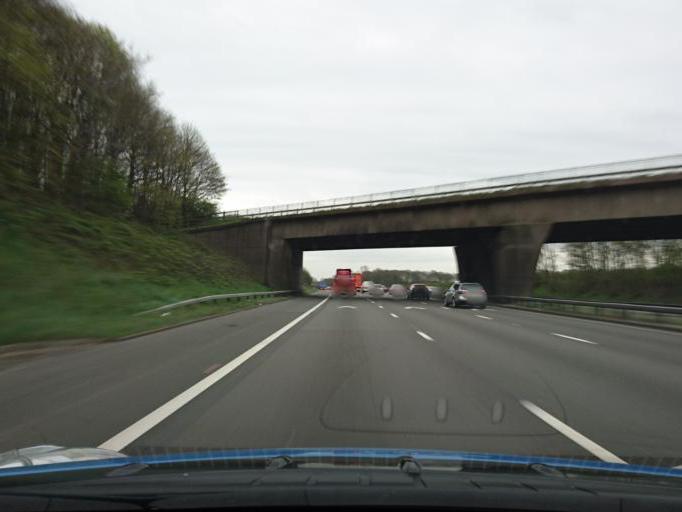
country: GB
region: England
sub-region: Staffordshire
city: Barlaston
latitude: 52.9248
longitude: -2.2077
